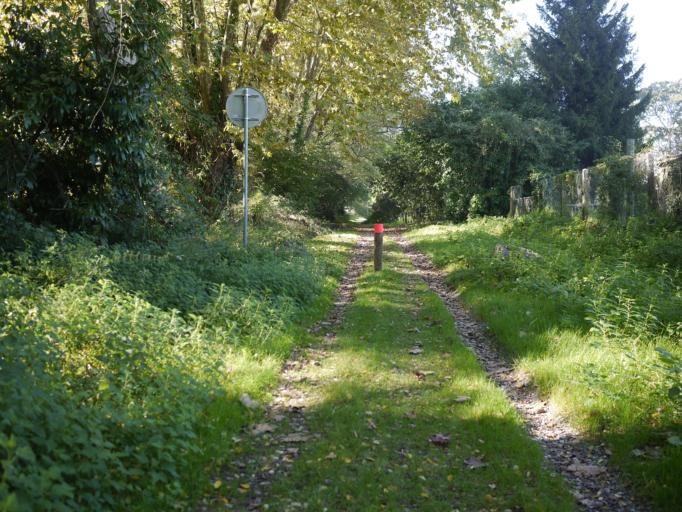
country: FR
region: Aquitaine
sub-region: Departement des Landes
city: Saint-Paul-les-Dax
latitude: 43.7241
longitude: -1.0699
